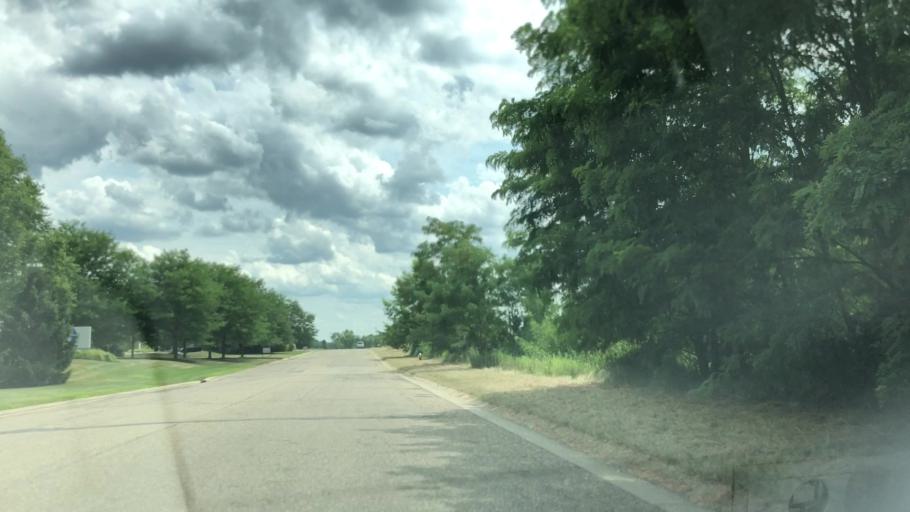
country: US
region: Ohio
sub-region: Summit County
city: Greensburg
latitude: 40.9034
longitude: -81.4461
